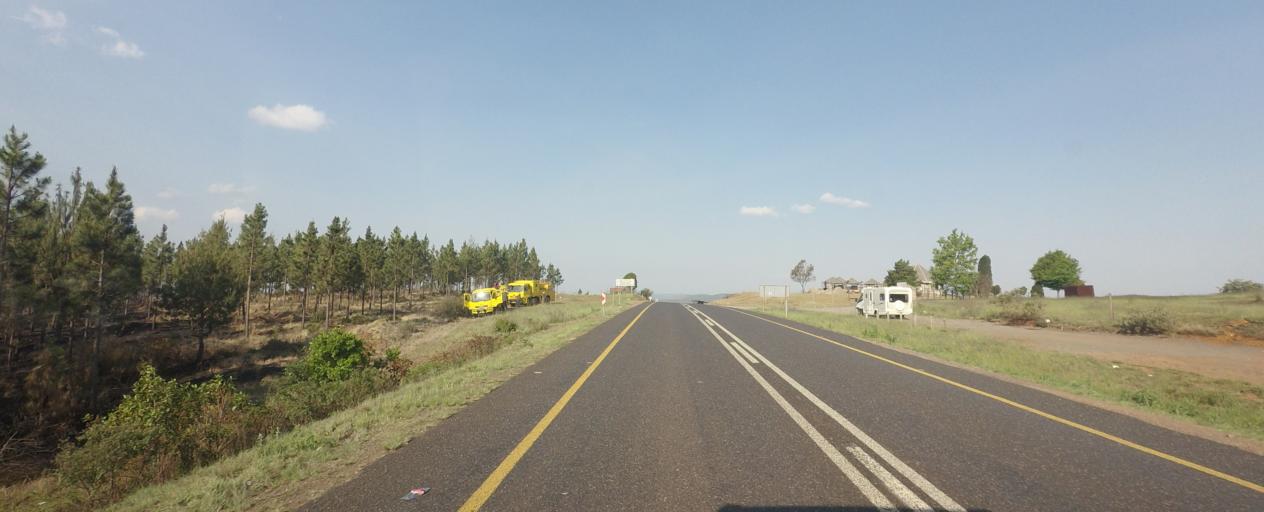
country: ZA
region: Mpumalanga
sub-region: Ehlanzeni District
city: Lydenburg
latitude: -25.1636
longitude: 30.6788
